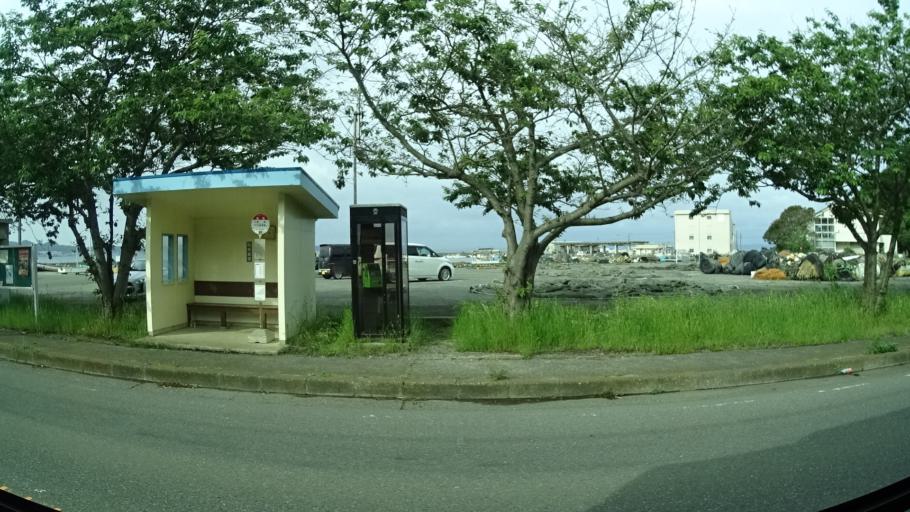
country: JP
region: Kanagawa
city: Miura
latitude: 35.1583
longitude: 139.6640
